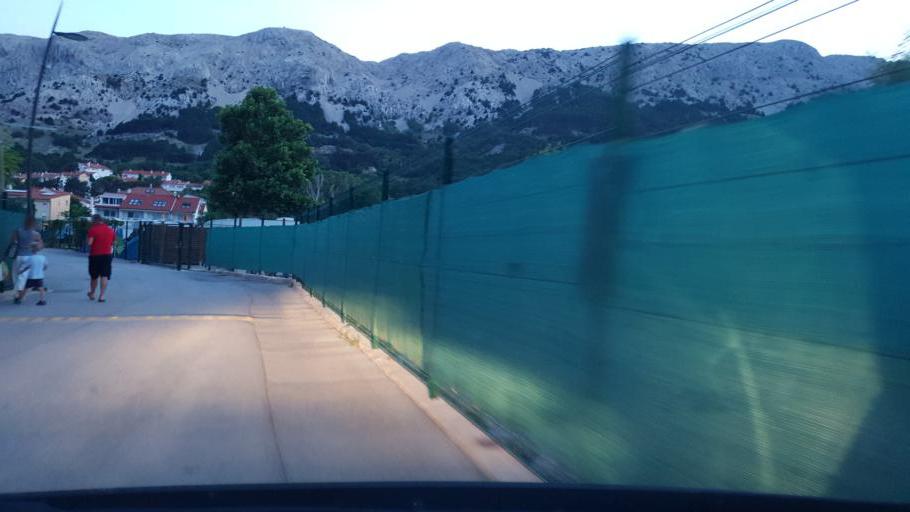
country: HR
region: Primorsko-Goranska
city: Punat
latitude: 44.9647
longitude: 14.7465
